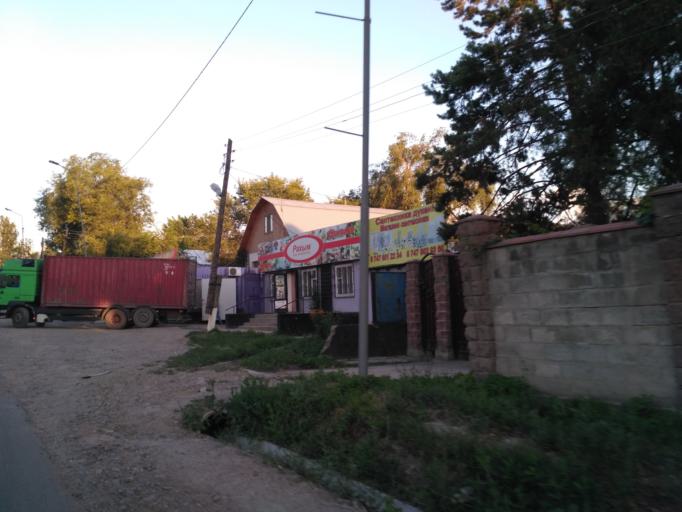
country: KZ
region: Almaty Qalasy
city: Almaty
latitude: 43.1753
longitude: 76.7620
